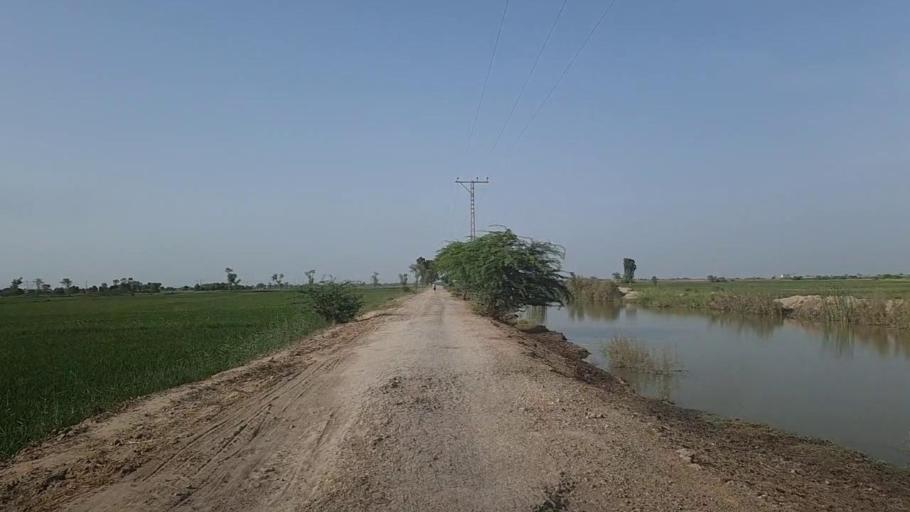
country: PK
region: Sindh
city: Sita Road
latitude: 27.1062
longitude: 67.8749
